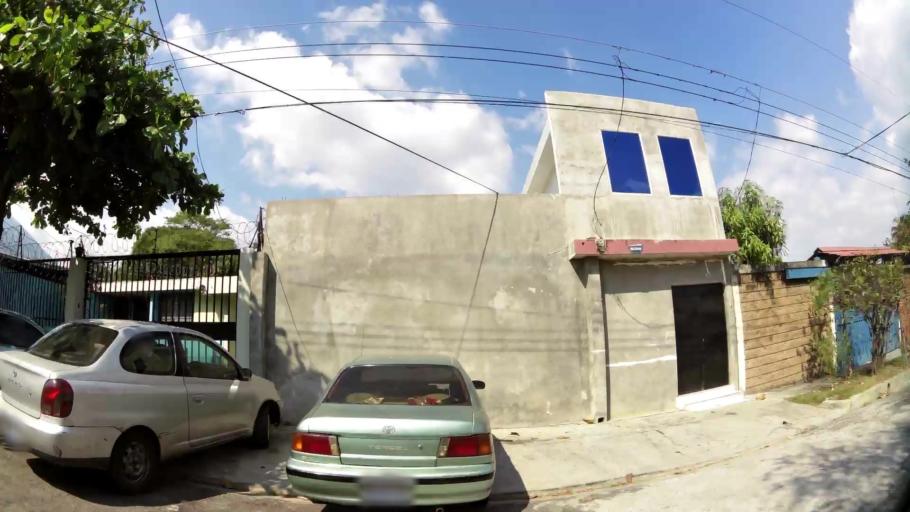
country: SV
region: San Salvador
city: Mejicanos
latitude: 13.7246
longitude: -89.2172
